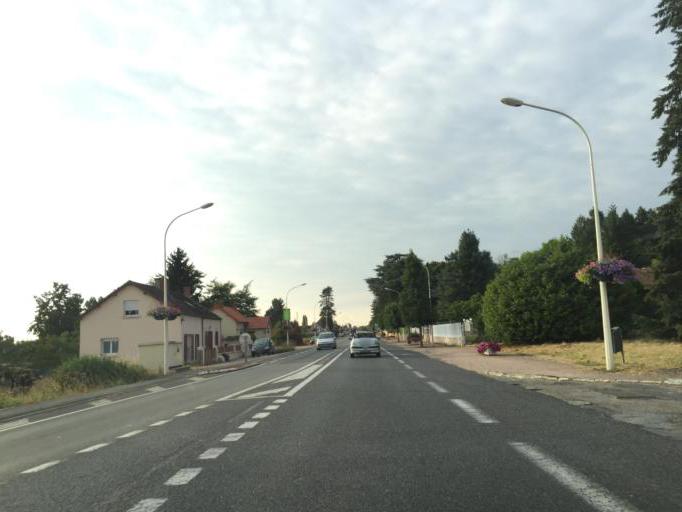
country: FR
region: Auvergne
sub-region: Departement de l'Allier
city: Varennes-sur-Allier
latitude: 46.3220
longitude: 3.3914
